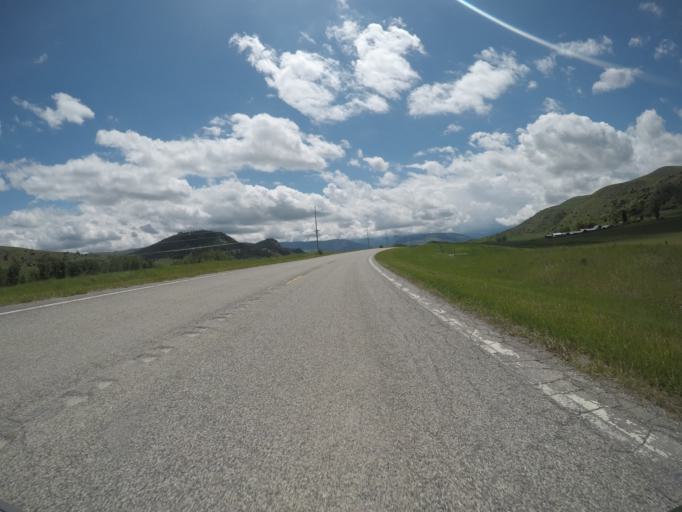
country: US
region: Montana
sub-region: Sweet Grass County
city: Big Timber
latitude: 45.6473
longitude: -110.1145
